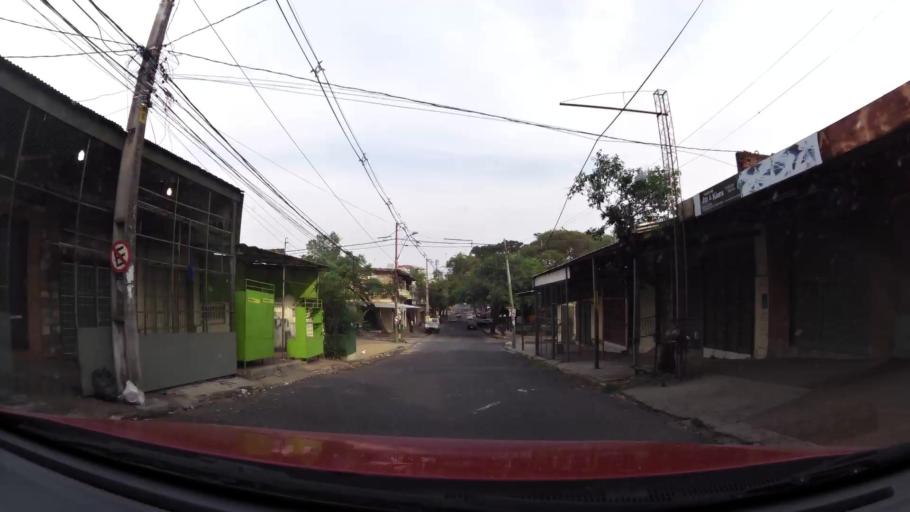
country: PY
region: Asuncion
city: Asuncion
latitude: -25.3017
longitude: -57.6231
